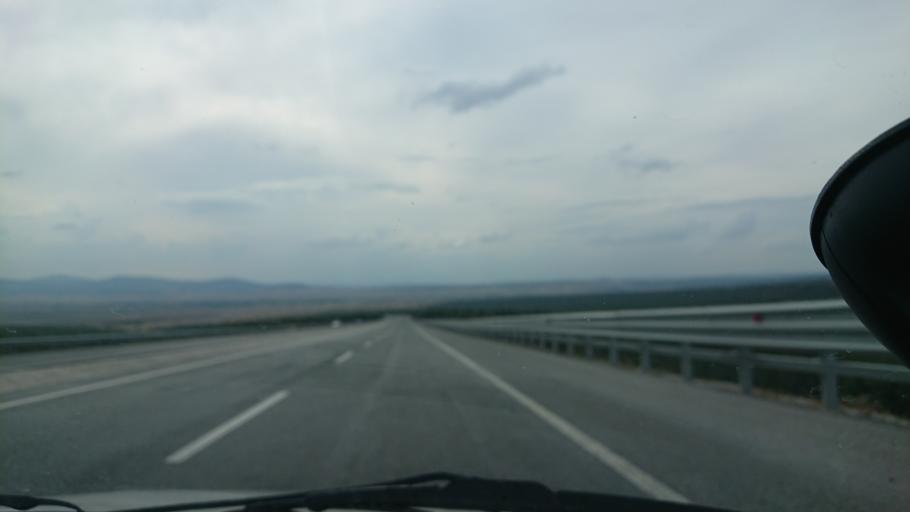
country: TR
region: Kuetahya
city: Aslanapa
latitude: 39.2771
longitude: 29.9111
